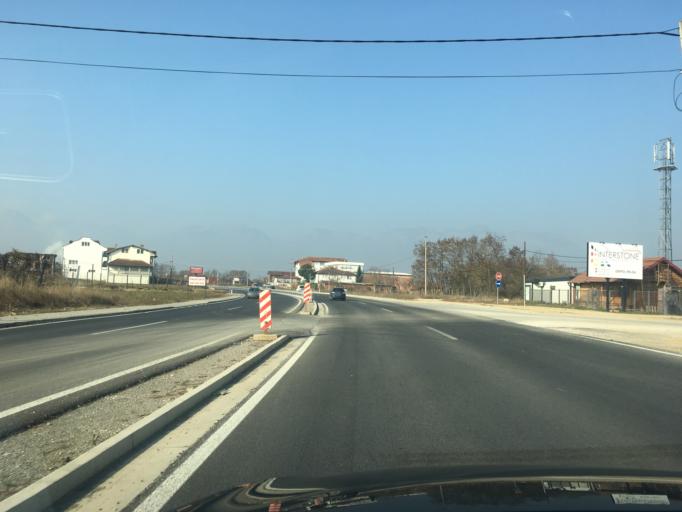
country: XK
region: Pec
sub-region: Komuna e Pejes
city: Dubova (Driloni)
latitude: 42.6541
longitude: 20.3997
